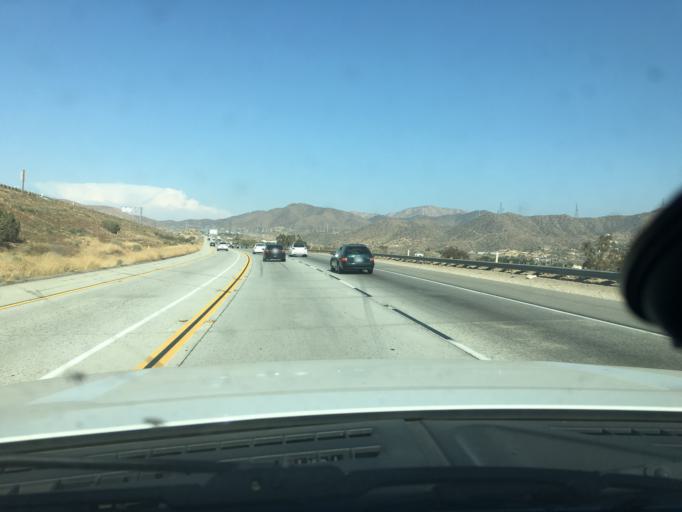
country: US
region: California
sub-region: Los Angeles County
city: Vincent
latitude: 34.4852
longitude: -118.1544
